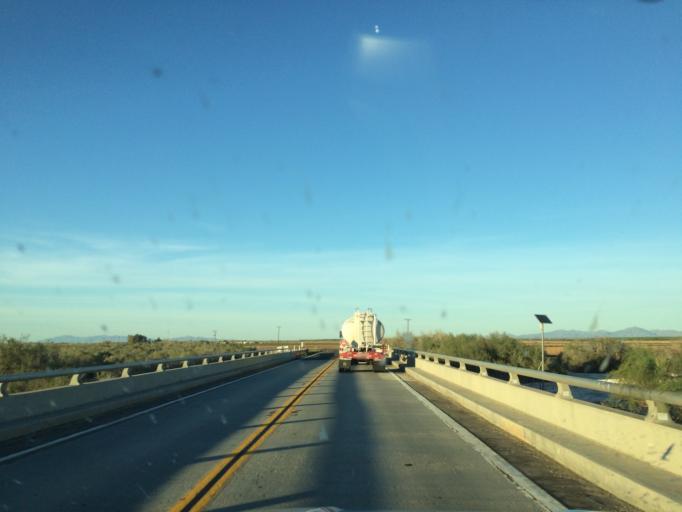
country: US
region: California
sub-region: Riverside County
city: Mesa Verde
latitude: 33.3610
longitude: -114.7233
